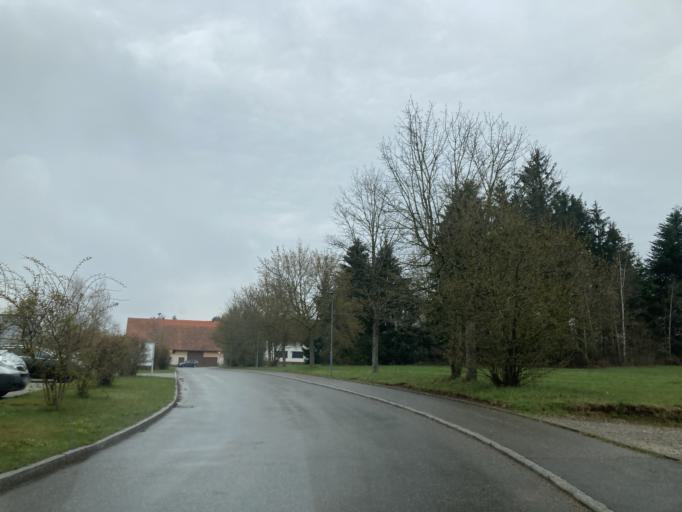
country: DE
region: Baden-Wuerttemberg
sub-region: Freiburg Region
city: Aichhalden
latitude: 48.2396
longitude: 8.4275
